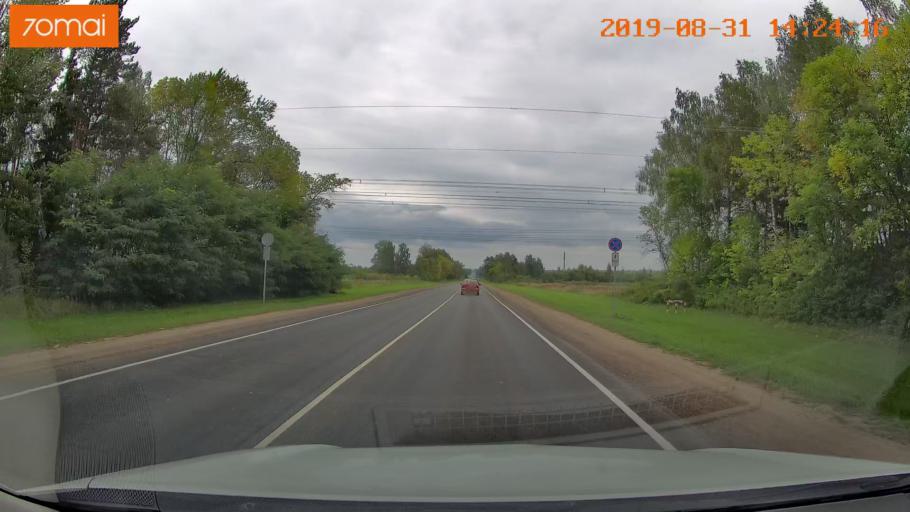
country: RU
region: Smolensk
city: Yekimovichi
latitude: 54.1019
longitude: 33.2519
